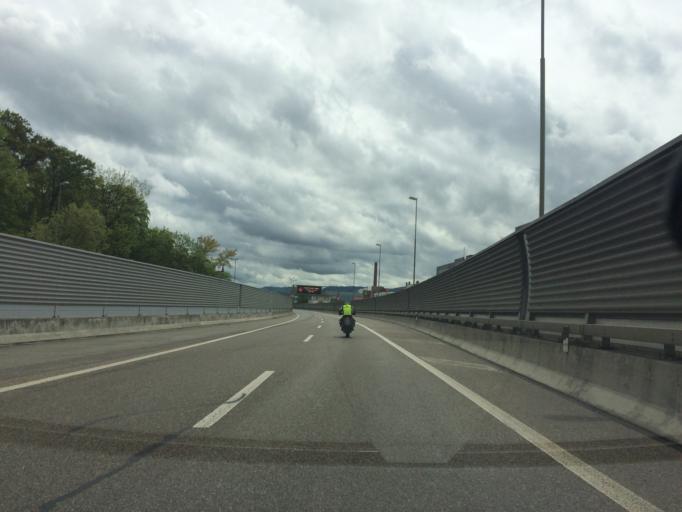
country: CH
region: Zurich
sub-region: Bezirk Zuerich
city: Zuerich (Kreis 3) / Alt-Wiedikon
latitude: 47.3636
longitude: 8.5226
